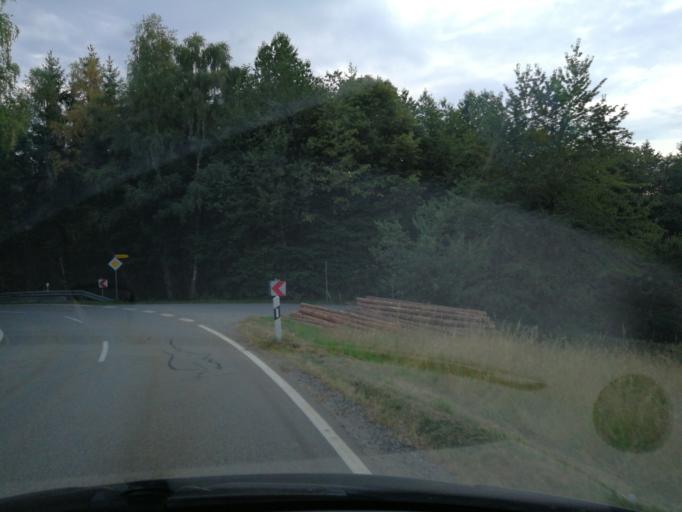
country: DE
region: Bavaria
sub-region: Lower Bavaria
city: Haibach
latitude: 49.0279
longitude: 12.7451
